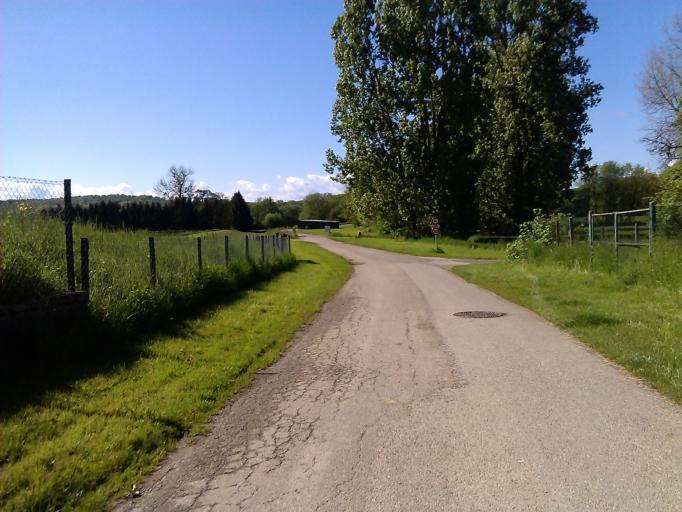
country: FR
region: Alsace
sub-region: Departement du Haut-Rhin
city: Aspach
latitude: 47.6705
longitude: 7.1990
